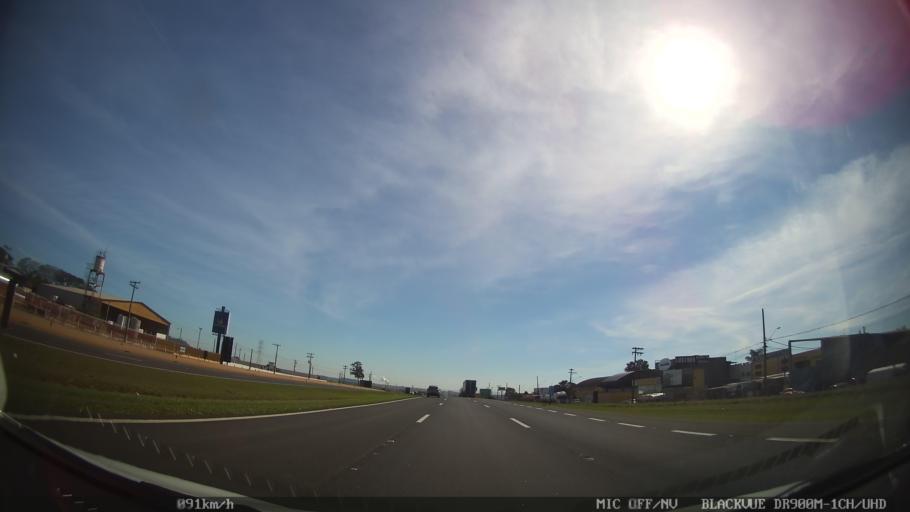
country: BR
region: Sao Paulo
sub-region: Pirassununga
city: Pirassununga
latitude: -22.0354
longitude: -47.4330
